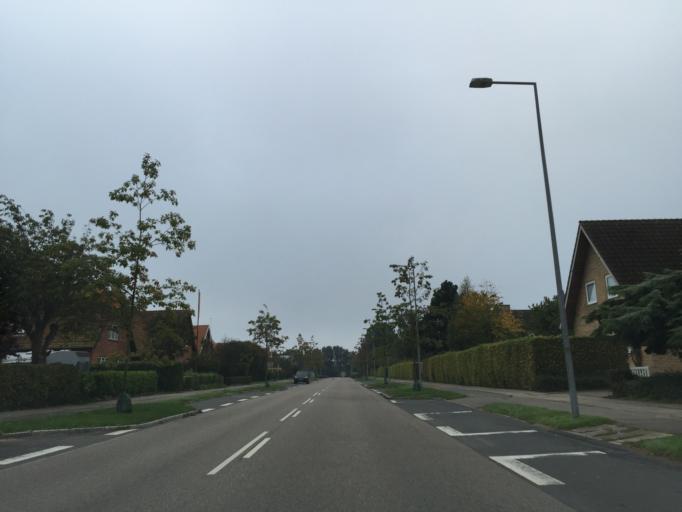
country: DK
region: South Denmark
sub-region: Sonderborg Kommune
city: Sonderborg
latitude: 54.9046
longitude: 9.8017
